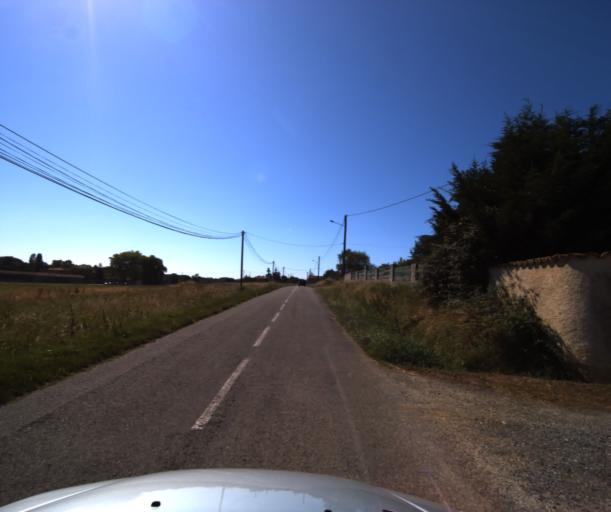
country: FR
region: Midi-Pyrenees
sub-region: Departement de la Haute-Garonne
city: Eaunes
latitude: 43.4199
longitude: 1.3492
